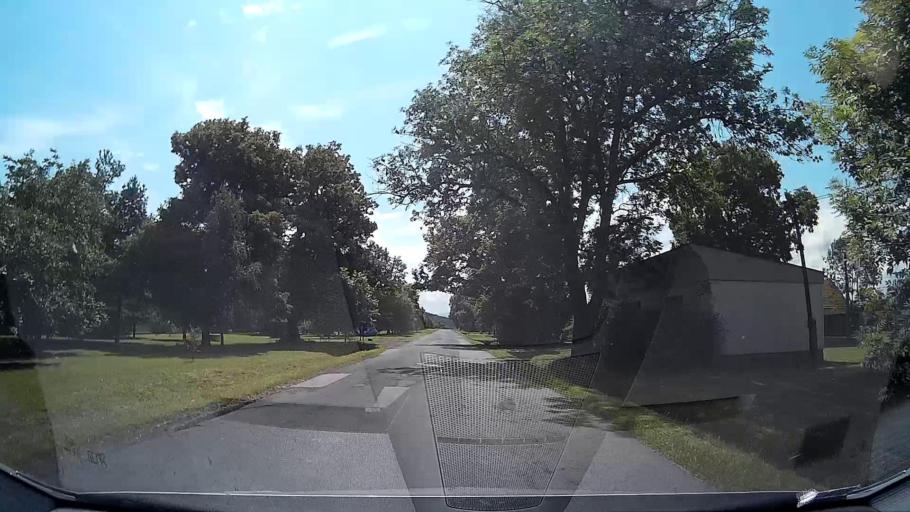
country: SK
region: Banskobystricky
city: Fil'akovo
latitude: 48.3272
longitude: 19.8168
